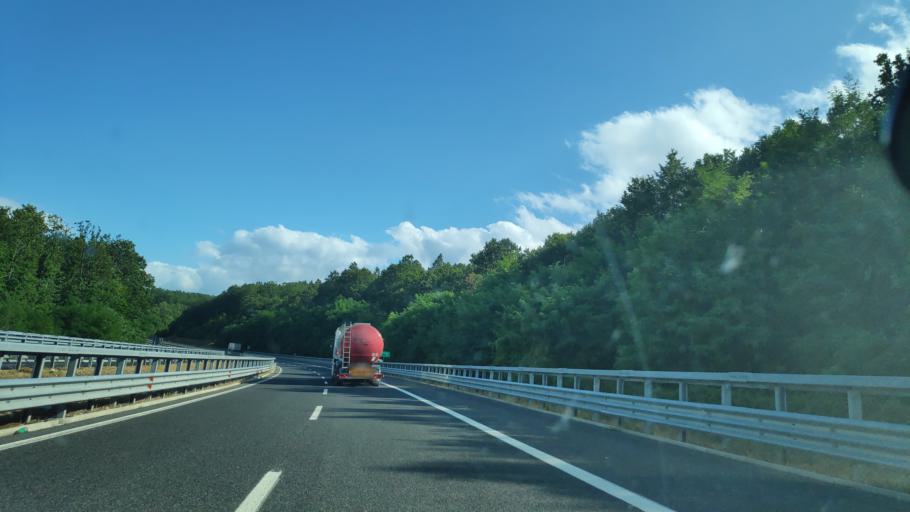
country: IT
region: Campania
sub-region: Provincia di Salerno
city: Casalbuono
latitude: 40.2395
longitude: 15.6598
